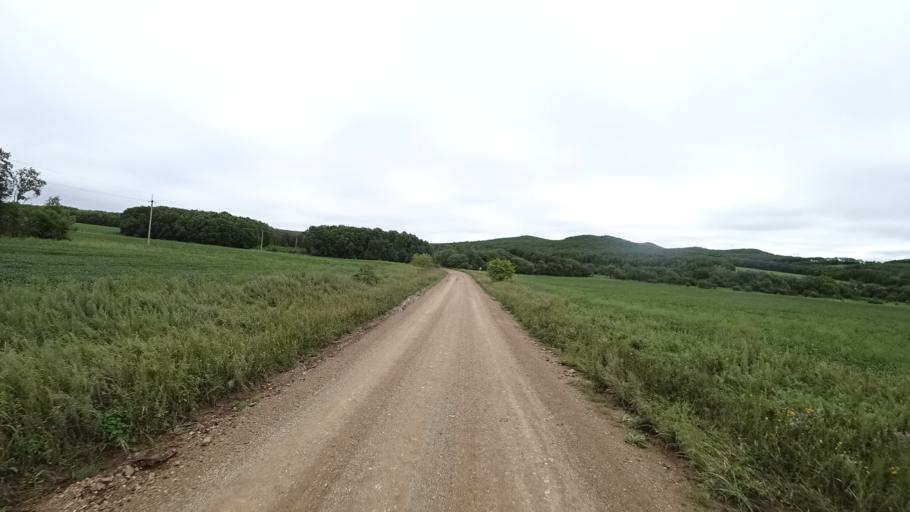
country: RU
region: Primorskiy
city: Lyalichi
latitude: 44.0583
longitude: 132.4775
